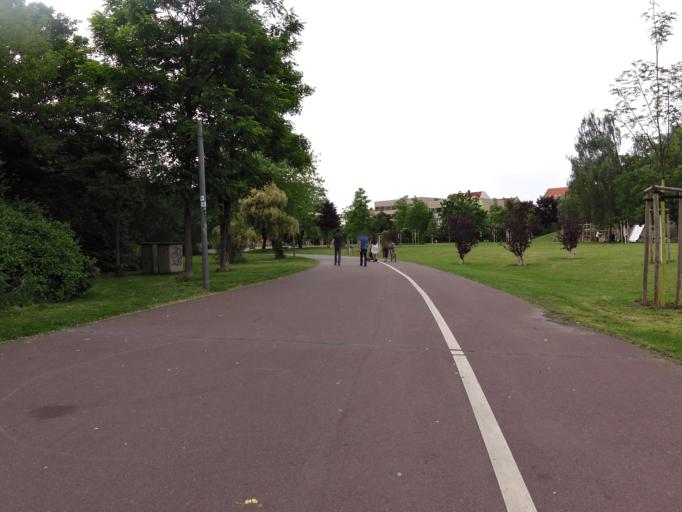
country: DE
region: Saxony
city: Leipzig
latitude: 51.3438
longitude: 12.4024
